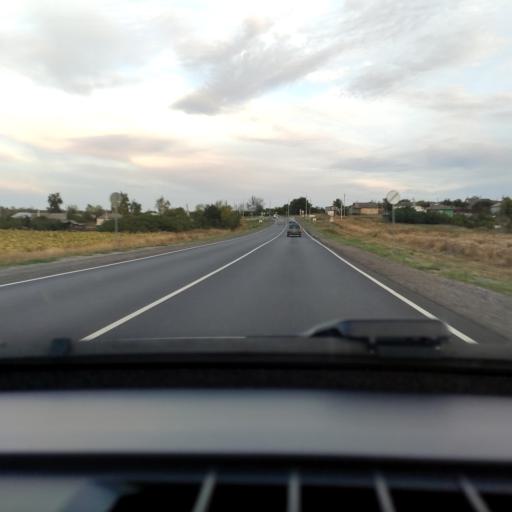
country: RU
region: Voronezj
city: Panino
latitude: 51.4715
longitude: 40.0277
